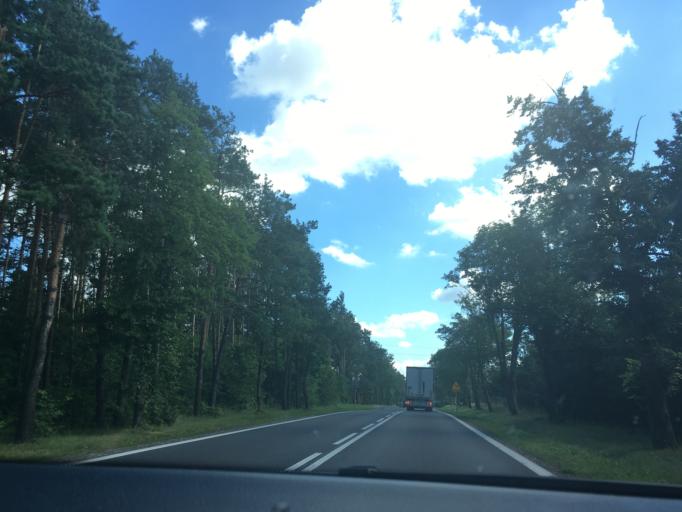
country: PL
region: Podlasie
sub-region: Powiat sokolski
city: Suchowola
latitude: 53.6639
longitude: 23.1246
